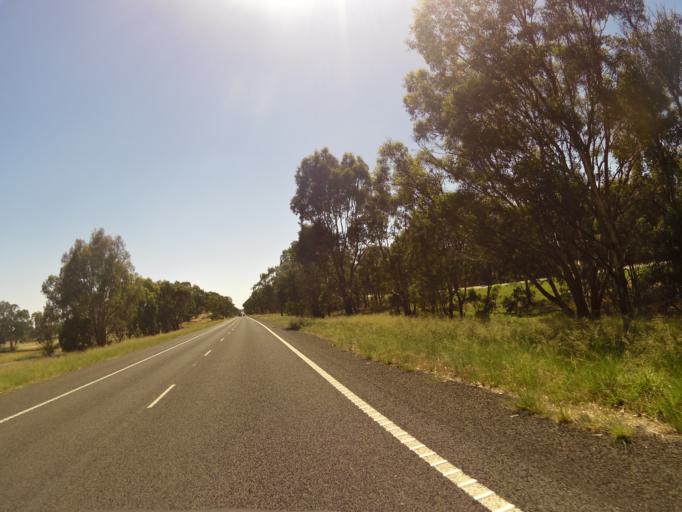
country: AU
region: Victoria
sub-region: Greater Shepparton
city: Shepparton
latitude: -36.8122
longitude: 145.4536
